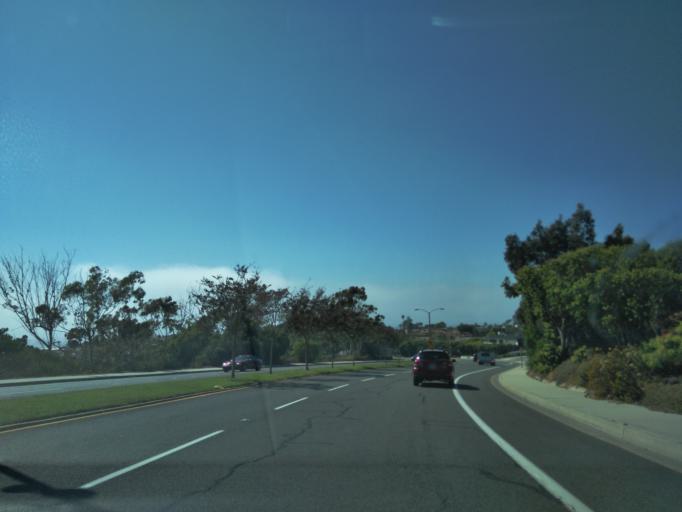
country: US
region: California
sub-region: Orange County
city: Dana Point
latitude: 33.4871
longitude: -117.7243
